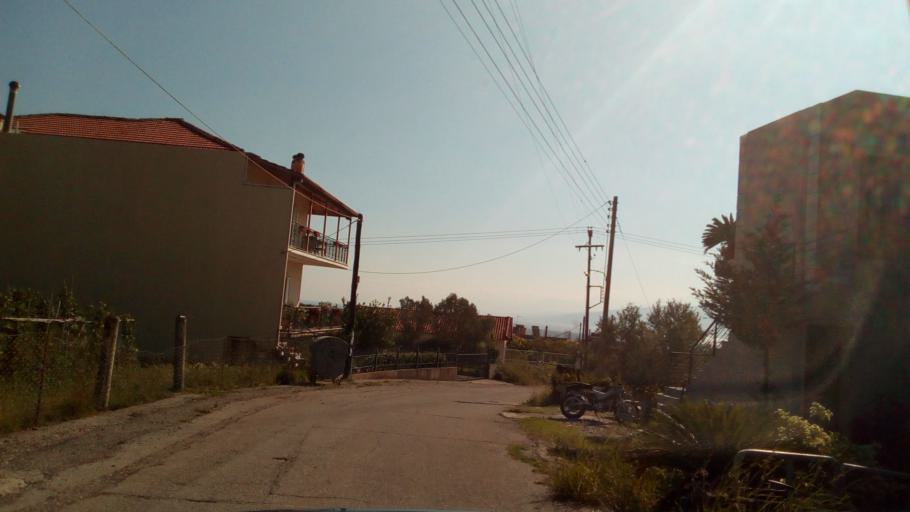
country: GR
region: West Greece
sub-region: Nomos Aitolias kai Akarnanias
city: Nafpaktos
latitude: 38.4195
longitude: 21.8703
